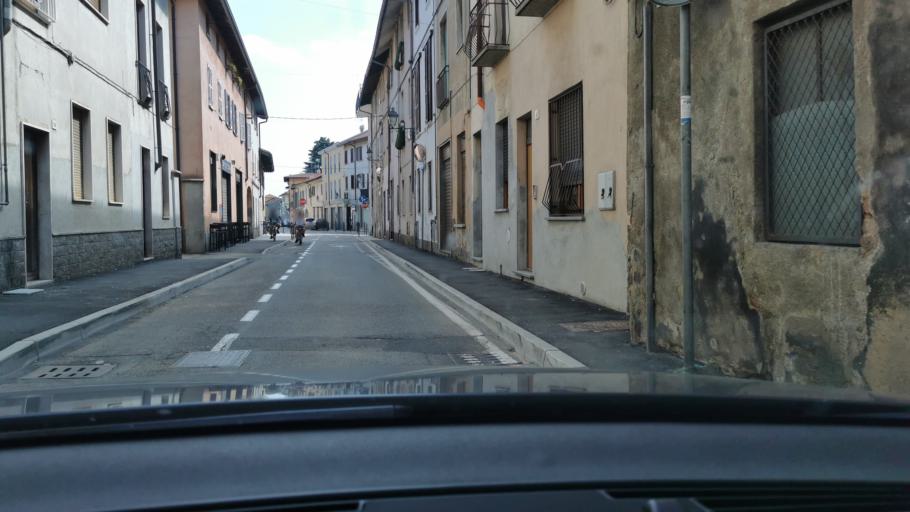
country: IT
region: Lombardy
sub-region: Provincia di Como
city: Turate
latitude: 45.6573
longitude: 9.0020
